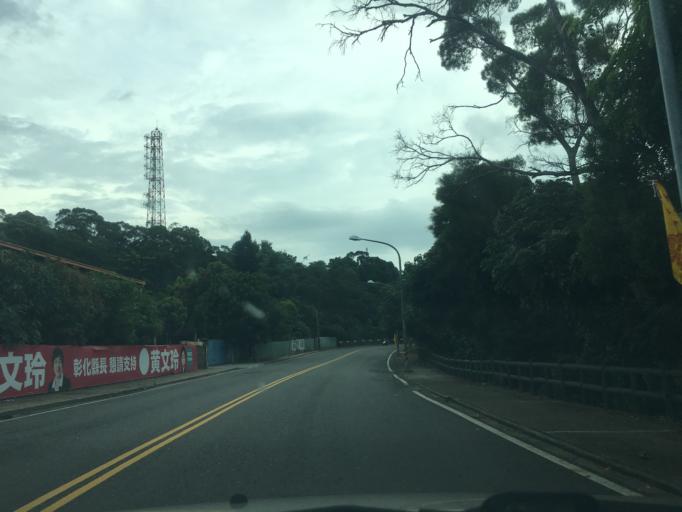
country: TW
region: Taiwan
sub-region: Changhua
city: Chang-hua
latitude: 24.0617
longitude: 120.5727
